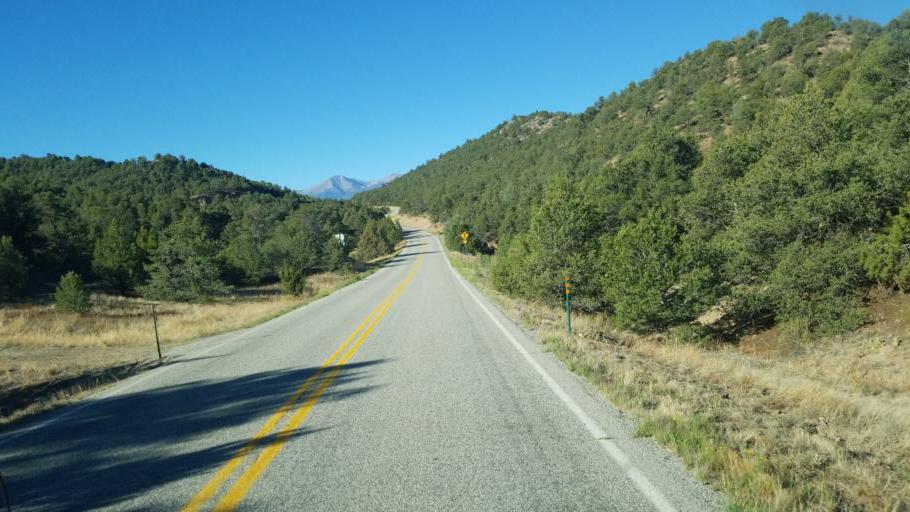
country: US
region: Colorado
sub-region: Custer County
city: Westcliffe
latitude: 38.3815
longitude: -105.5819
